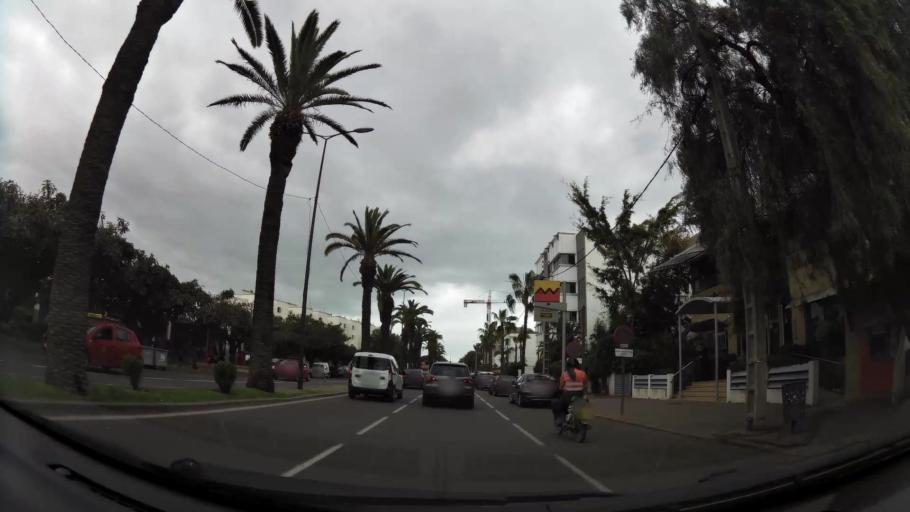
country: MA
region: Grand Casablanca
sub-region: Casablanca
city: Casablanca
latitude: 33.5659
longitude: -7.6380
